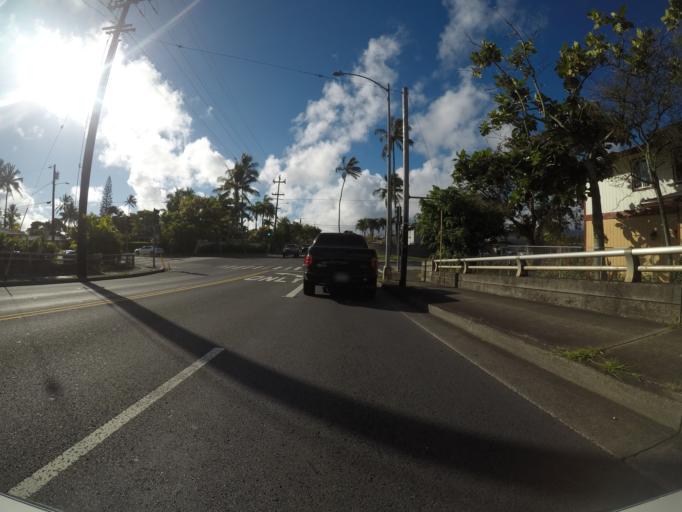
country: US
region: Hawaii
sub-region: Honolulu County
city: Kailua
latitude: 21.4089
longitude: -157.7540
